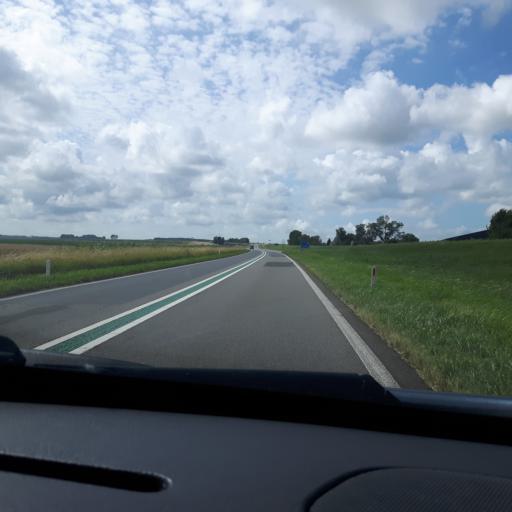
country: NL
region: Zeeland
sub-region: Gemeente Goes
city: Goes
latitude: 51.5772
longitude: 3.8186
